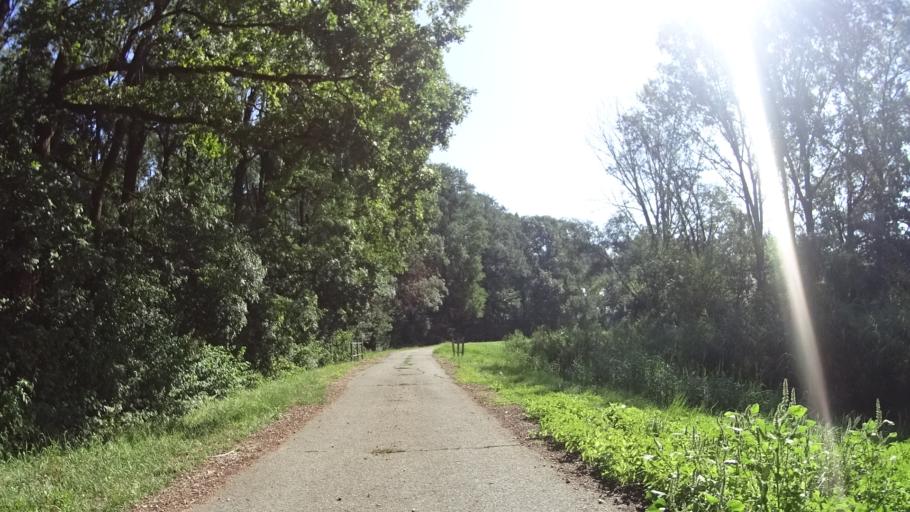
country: CZ
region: South Moravian
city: Hodonin
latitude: 48.8165
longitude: 17.1249
